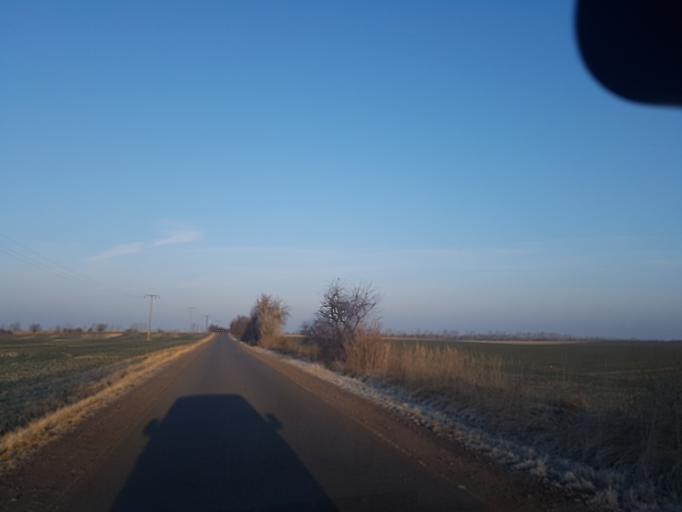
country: DE
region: Brandenburg
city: Niedergorsdorf
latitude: 51.9450
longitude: 13.0016
